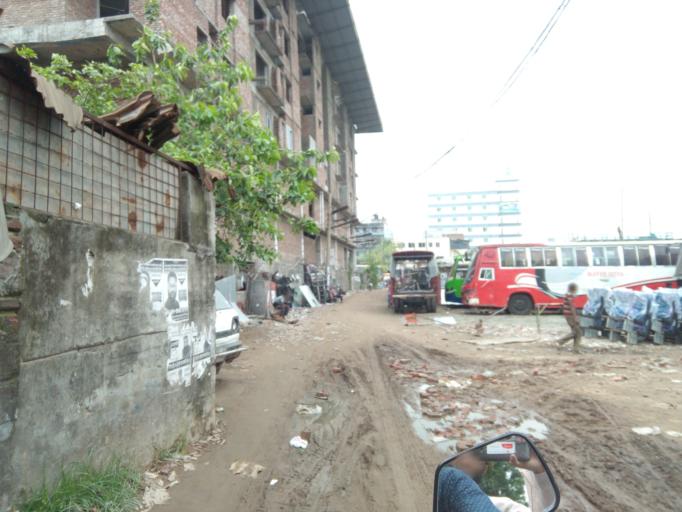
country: BD
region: Dhaka
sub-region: Dhaka
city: Dhaka
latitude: 23.7116
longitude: 90.4507
